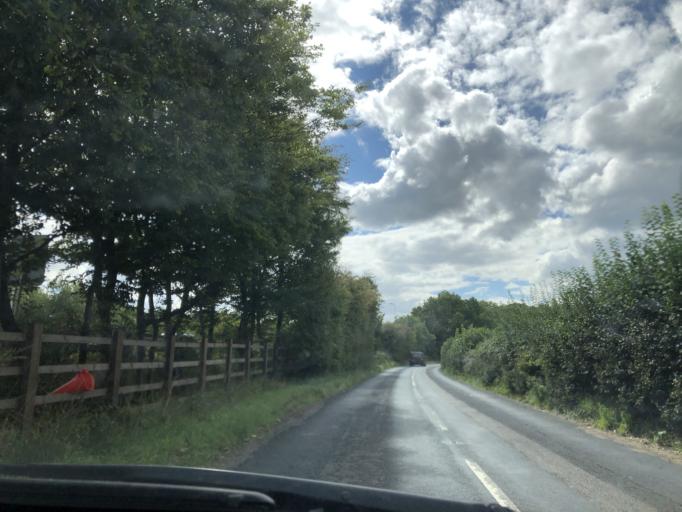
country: GB
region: England
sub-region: Kent
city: Halstead
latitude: 51.2963
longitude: 0.1440
